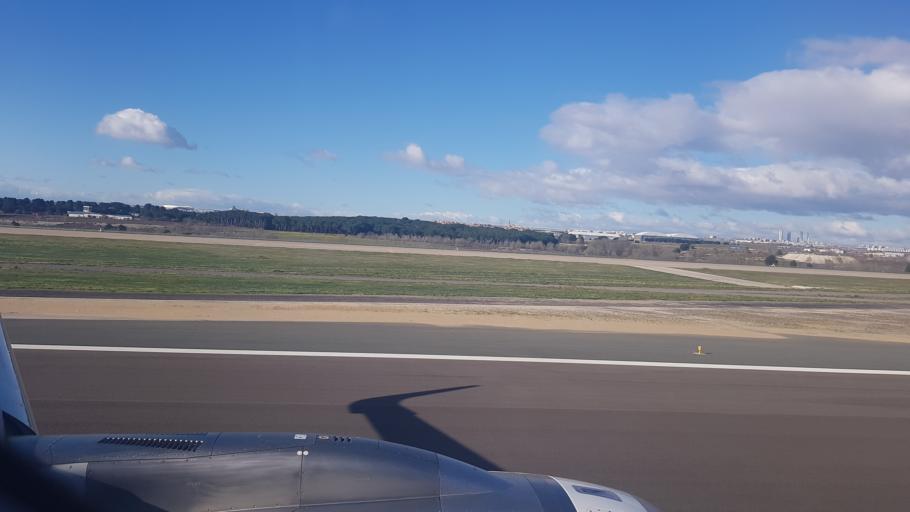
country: ES
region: Madrid
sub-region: Provincia de Madrid
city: Paracuellos de Jarama
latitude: 40.4853
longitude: -3.5479
